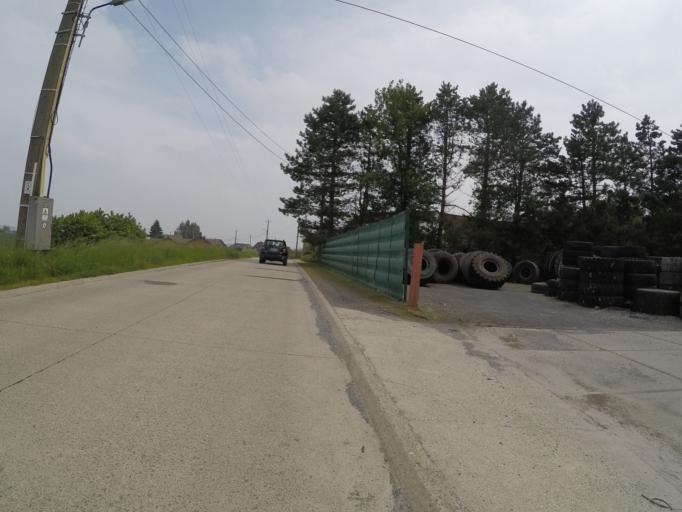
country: BE
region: Wallonia
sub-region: Province de Namur
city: Assesse
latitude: 50.3391
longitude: 5.0457
